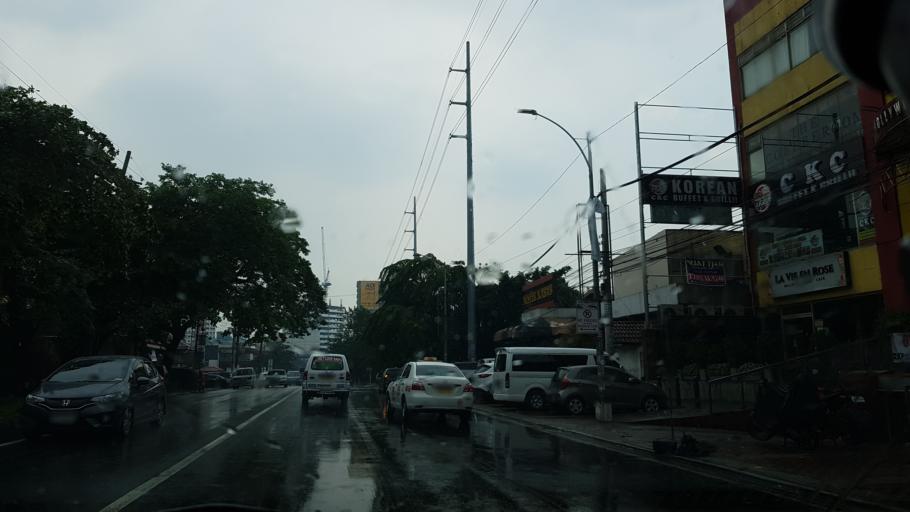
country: PH
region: Calabarzon
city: Del Monte
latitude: 14.6415
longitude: 121.0268
